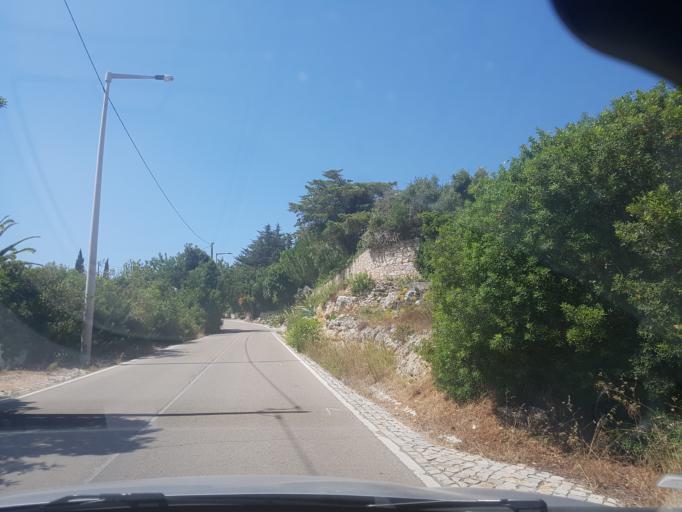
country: PT
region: Faro
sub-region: Lagoa
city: Carvoeiro
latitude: 37.0911
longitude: -8.4414
